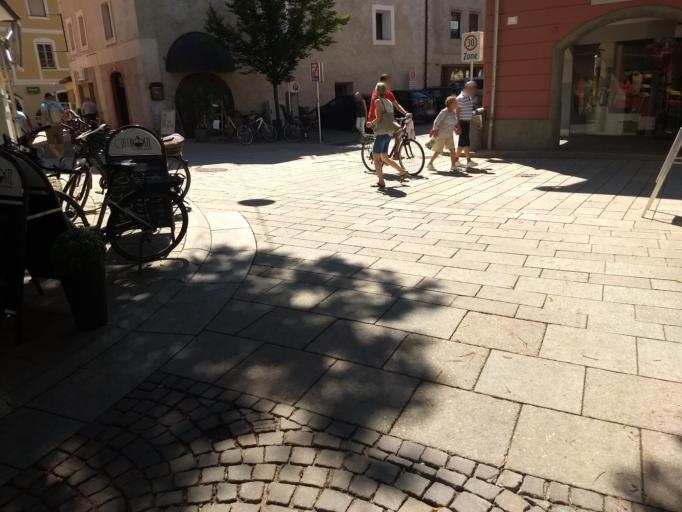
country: AT
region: Tyrol
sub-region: Politischer Bezirk Lienz
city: Lienz
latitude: 46.8294
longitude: 12.7642
